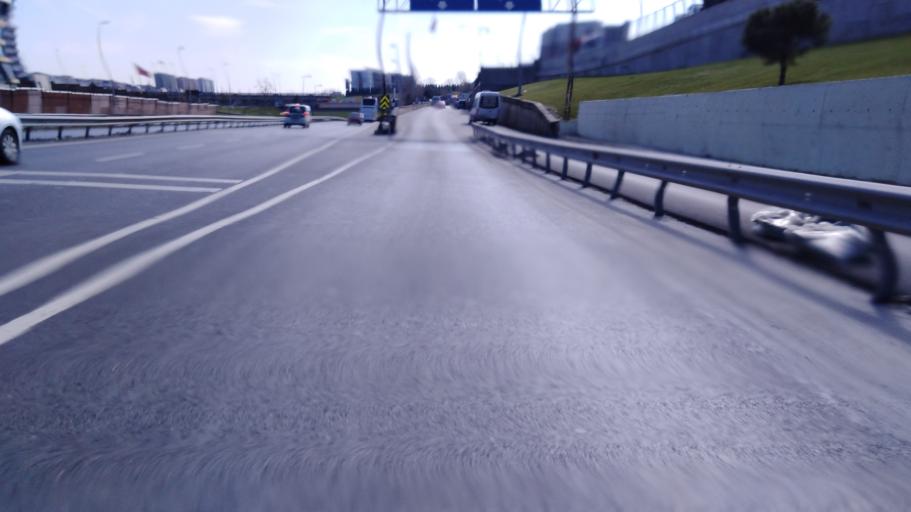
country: TR
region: Istanbul
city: Esenler
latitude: 41.0483
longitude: 28.8906
